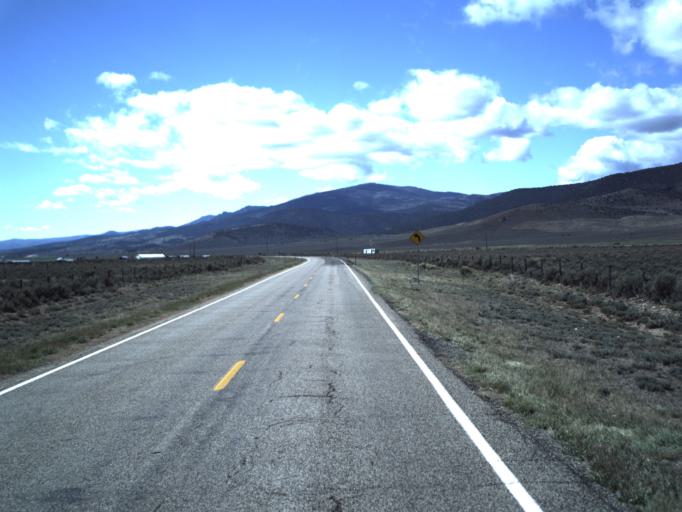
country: US
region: Utah
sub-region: Wayne County
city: Loa
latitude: 38.4768
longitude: -111.9002
